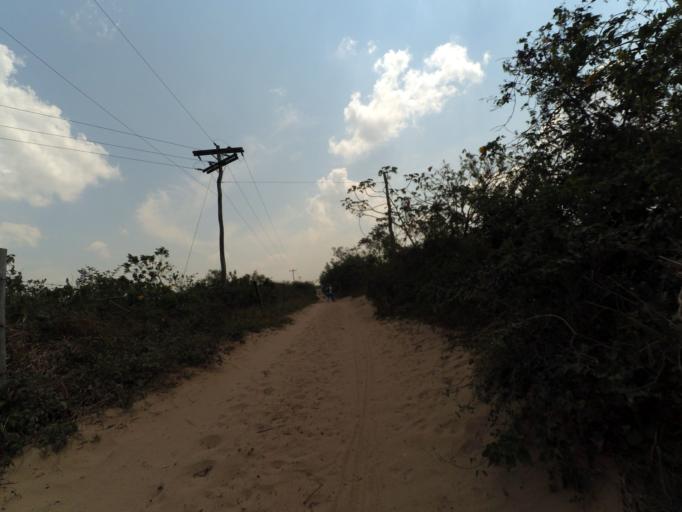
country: BO
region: Santa Cruz
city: Santa Cruz de la Sierra
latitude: -17.8842
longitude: -63.2048
